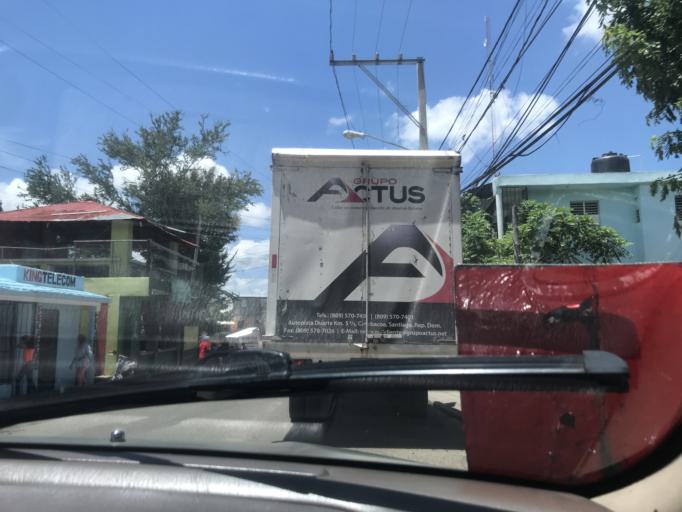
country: DO
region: Santiago
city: Santiago de los Caballeros
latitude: 19.4132
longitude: -70.6862
